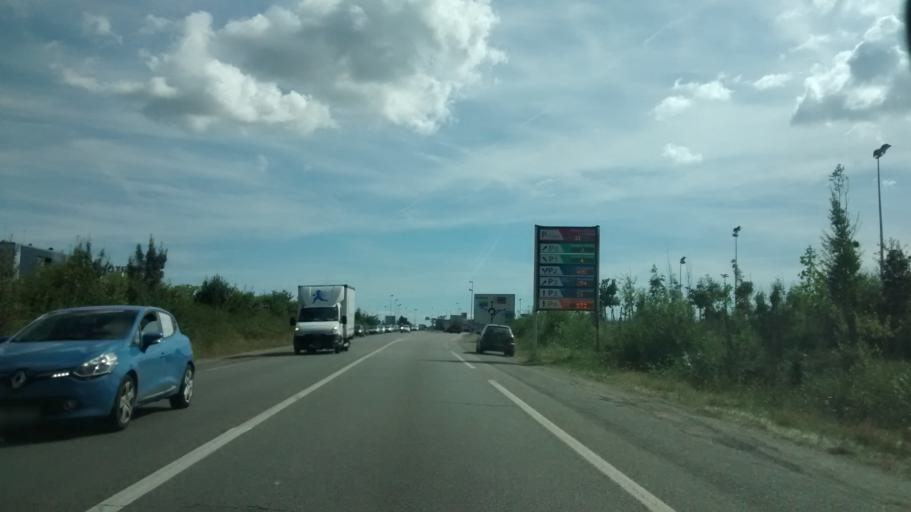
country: FR
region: Pays de la Loire
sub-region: Departement de la Loire-Atlantique
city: Bouguenais
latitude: 47.1617
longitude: -1.5968
